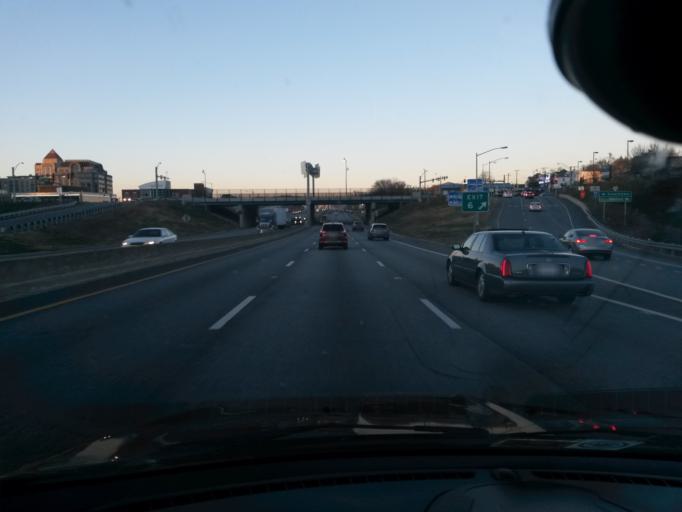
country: US
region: Virginia
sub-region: City of Roanoke
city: Cedar Bluff
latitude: 37.2654
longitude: -79.9373
